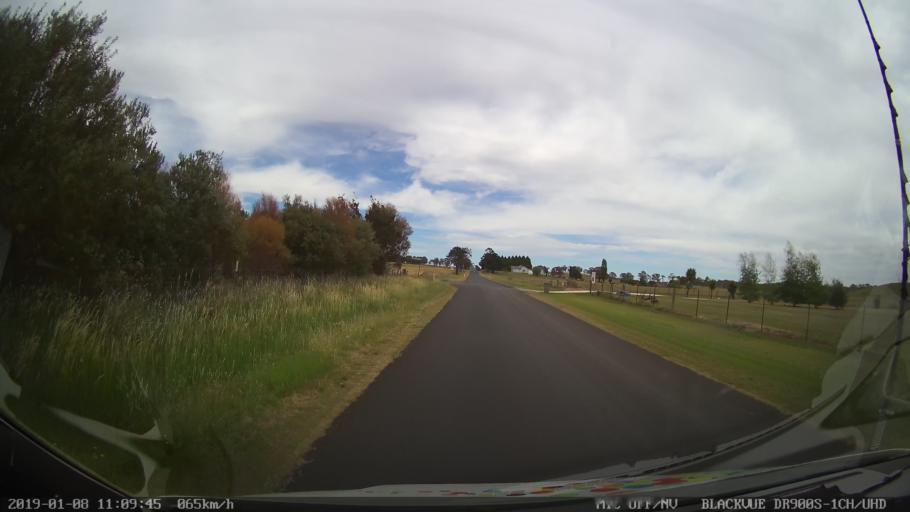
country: AU
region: New South Wales
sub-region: Guyra
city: Guyra
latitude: -30.2266
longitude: 151.6438
